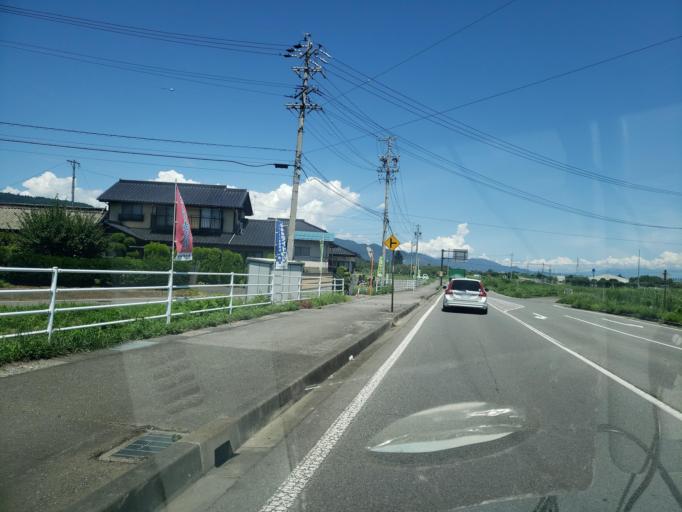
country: JP
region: Nagano
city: Nagano-shi
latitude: 36.5418
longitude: 138.1116
